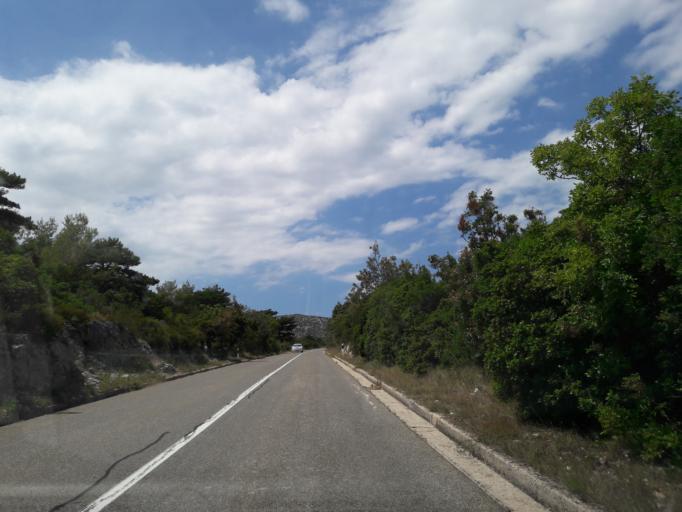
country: HR
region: Dubrovacko-Neretvanska
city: Orebic
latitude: 42.9704
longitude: 17.2796
